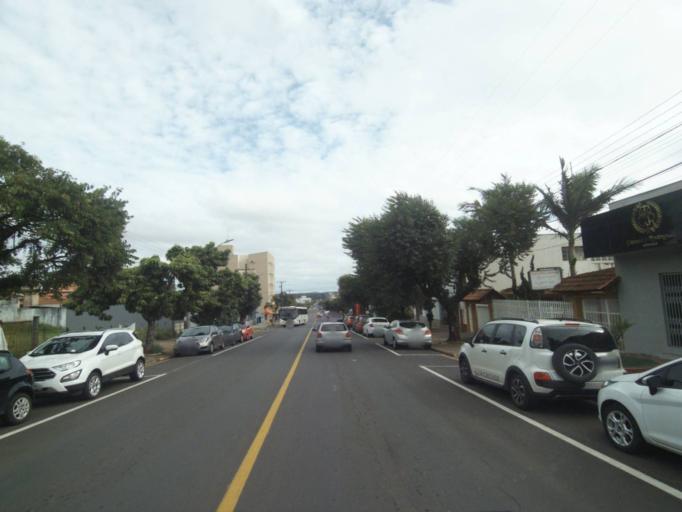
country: BR
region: Parana
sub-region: Telemaco Borba
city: Telemaco Borba
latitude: -24.3284
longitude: -50.6162
